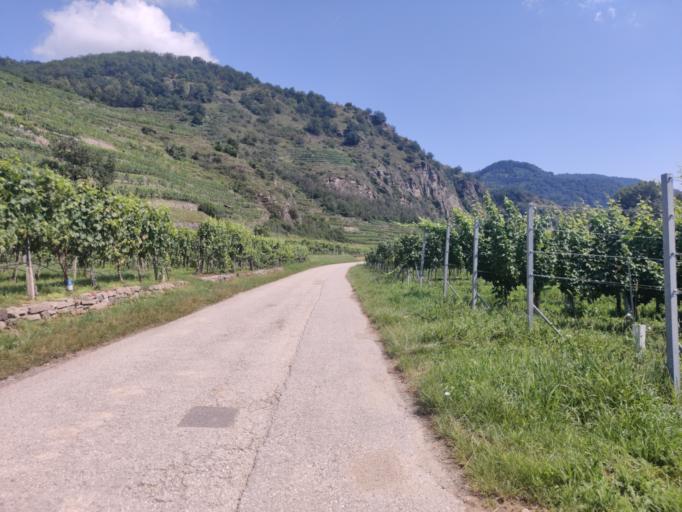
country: AT
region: Lower Austria
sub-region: Politischer Bezirk Krems
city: Durnstein
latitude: 48.4116
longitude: 15.4952
